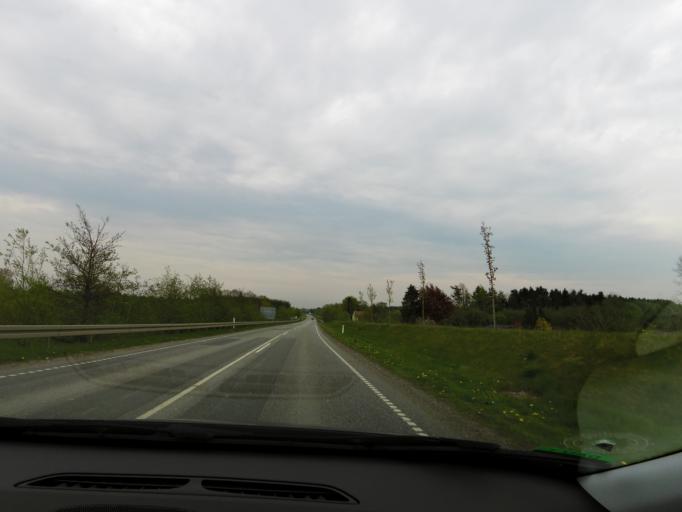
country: DK
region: South Denmark
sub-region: Faaborg-Midtfyn Kommune
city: Arslev
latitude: 55.3050
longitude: 10.4391
